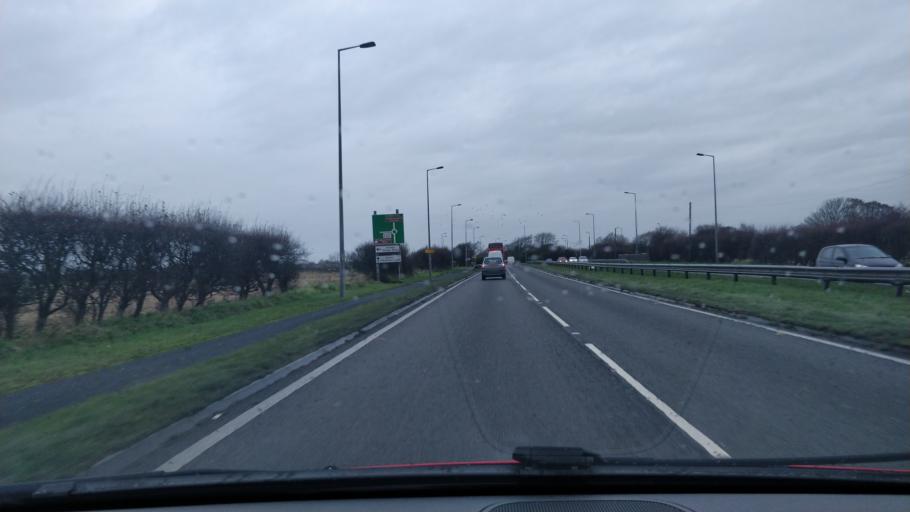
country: GB
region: England
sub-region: Sefton
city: Hightown
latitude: 53.5419
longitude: -3.0484
